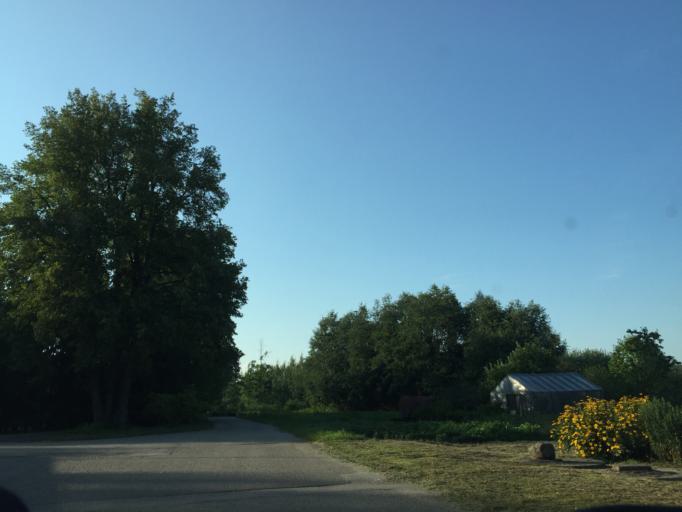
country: LV
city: Tervete
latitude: 56.4231
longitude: 23.5413
